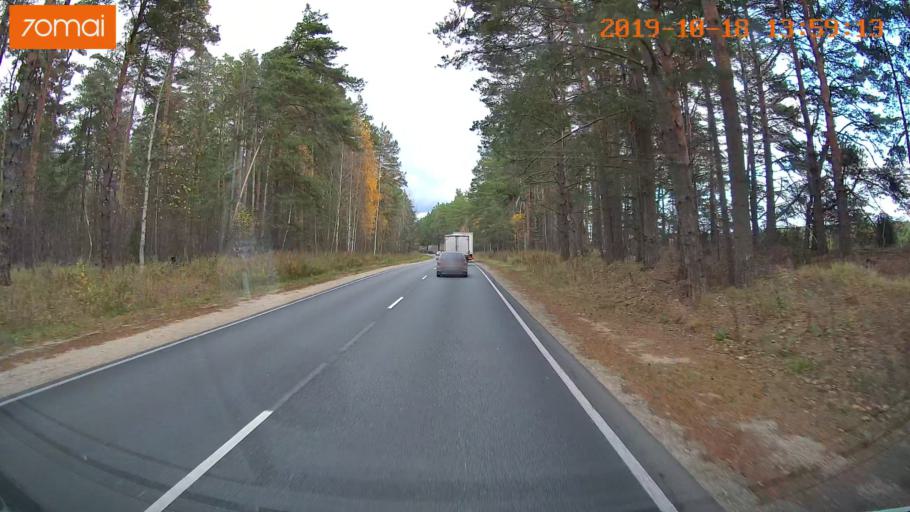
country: RU
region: Rjazan
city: Spas-Klepiki
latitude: 55.0921
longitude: 40.0614
